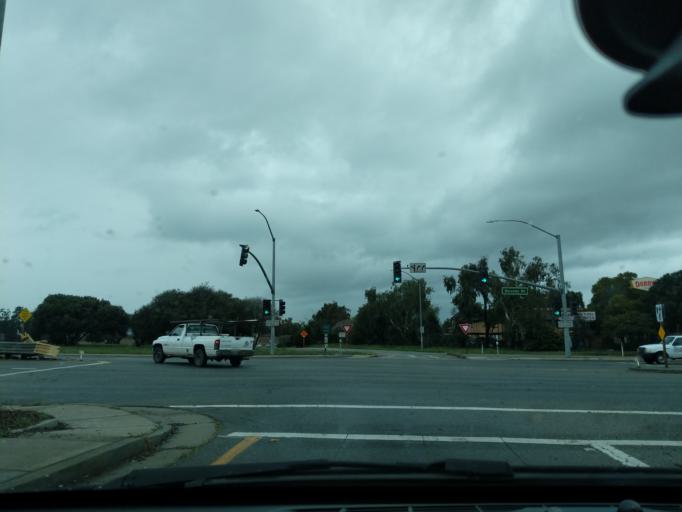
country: US
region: California
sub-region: Monterey County
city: Boronda
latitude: 36.7217
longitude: -121.6585
